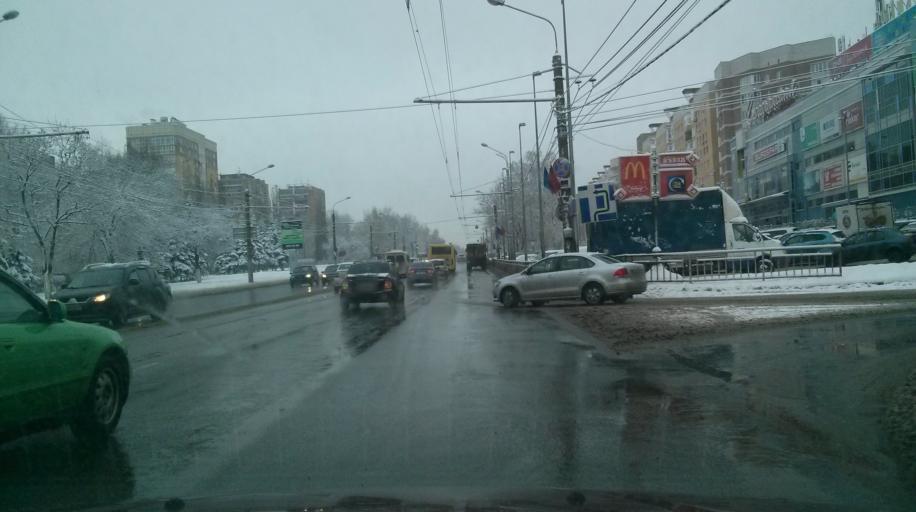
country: RU
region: Nizjnij Novgorod
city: Nizhniy Novgorod
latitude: 56.2354
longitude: 43.9531
